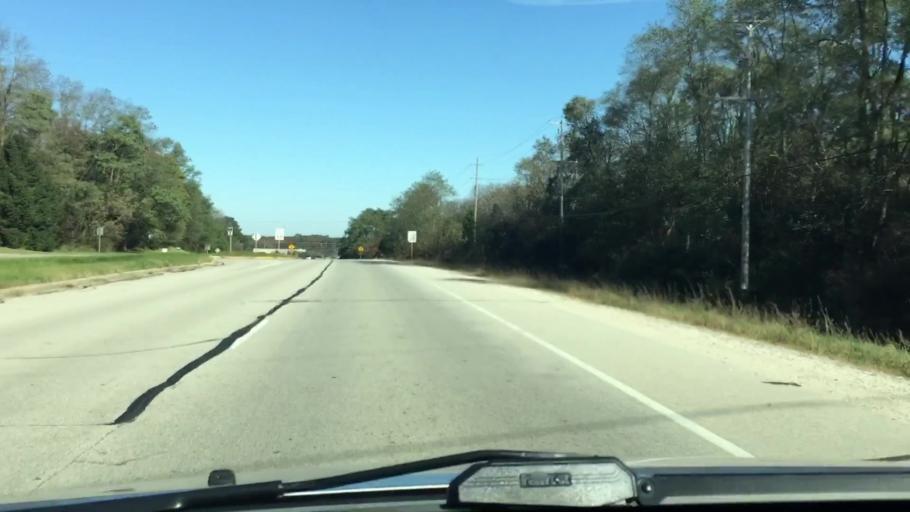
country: US
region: Wisconsin
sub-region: Waukesha County
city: Delafield
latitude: 43.0438
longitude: -88.3738
